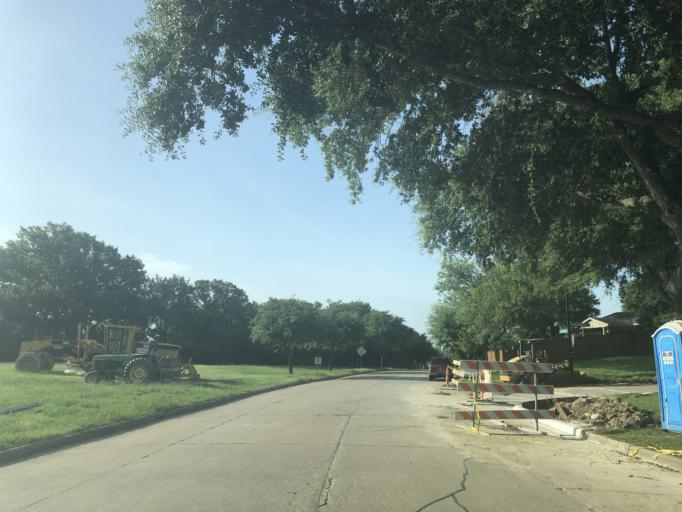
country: US
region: Texas
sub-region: Dallas County
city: Sunnyvale
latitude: 32.8401
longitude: -96.5817
